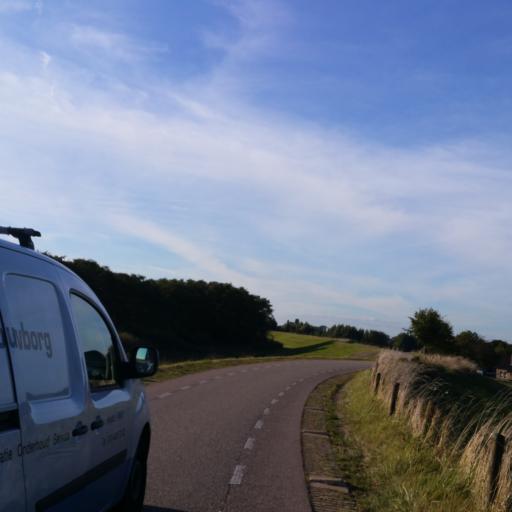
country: NL
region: Utrecht
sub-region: Gemeente IJsselstein
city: IJsselstein
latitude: 51.9756
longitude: 5.0225
